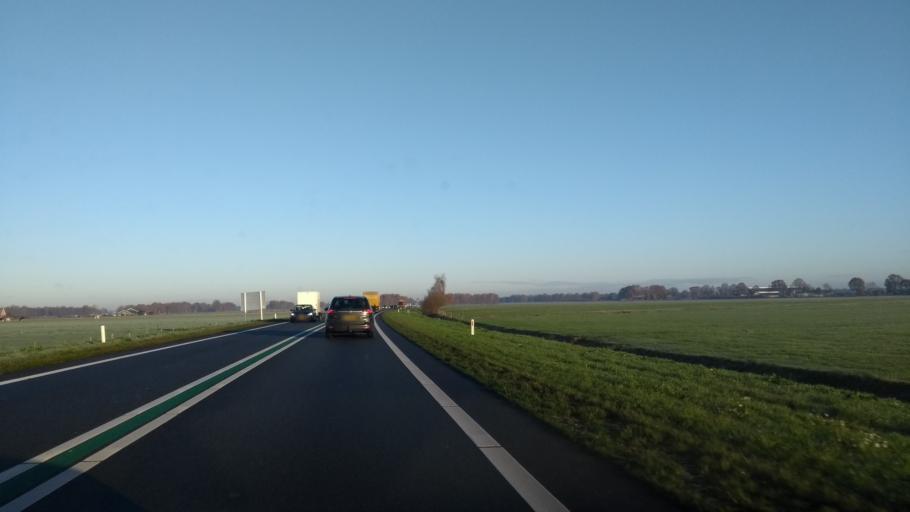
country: NL
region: Overijssel
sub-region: Gemeente Twenterand
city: Vriezenveen
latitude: 52.4223
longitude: 6.6305
